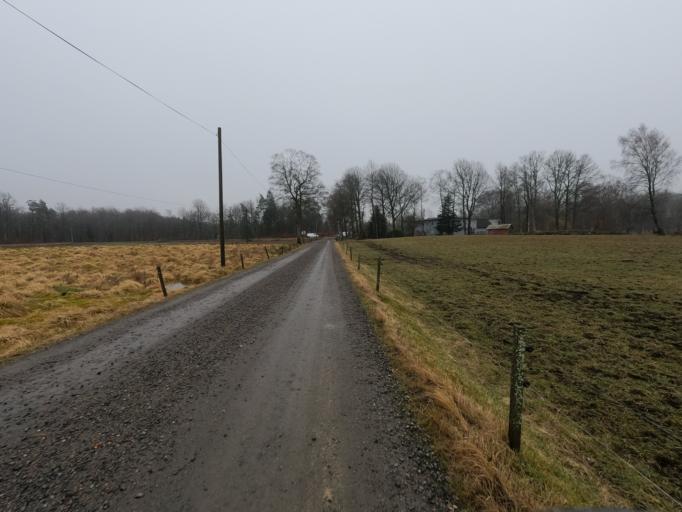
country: SE
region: Halland
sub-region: Hylte Kommun
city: Hyltebruk
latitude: 56.8019
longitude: 13.3301
